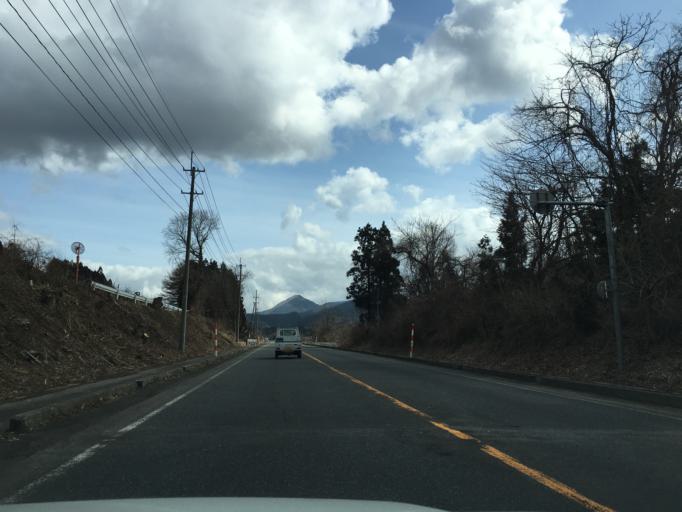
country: JP
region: Akita
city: Odate
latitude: 40.2205
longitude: 140.6087
